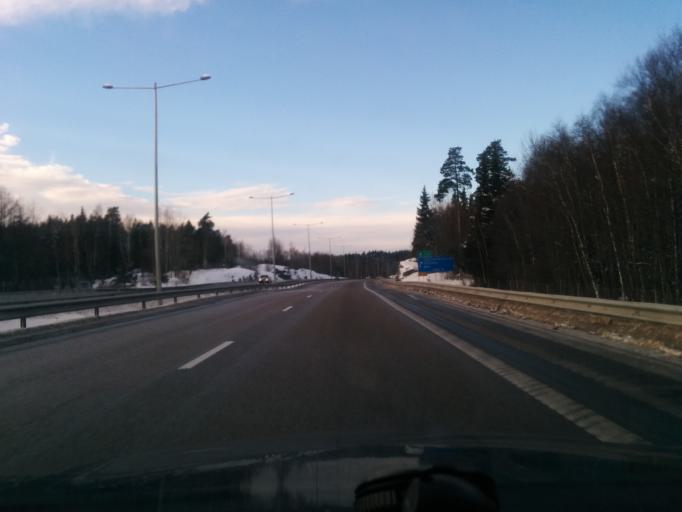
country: SE
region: Stockholm
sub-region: Upplands-Bro Kommun
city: Bro
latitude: 59.5271
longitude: 17.6410
